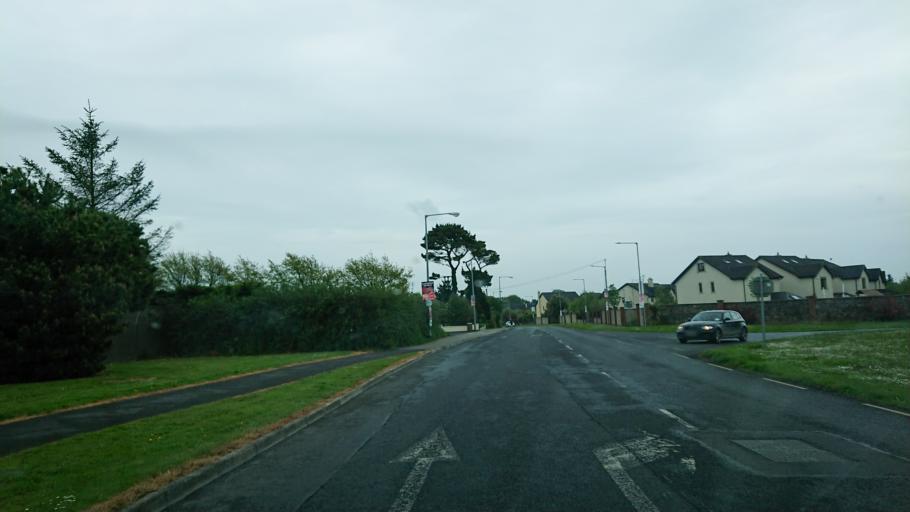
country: IE
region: Munster
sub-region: Waterford
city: Waterford
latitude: 52.2360
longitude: -7.0794
